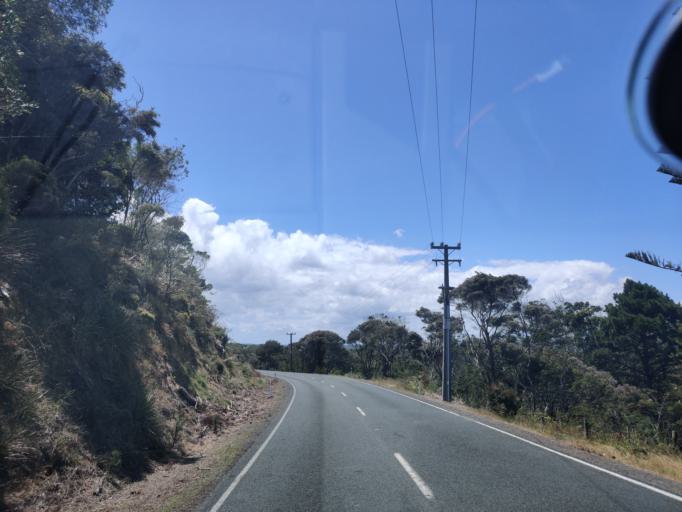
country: NZ
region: Northland
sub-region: Far North District
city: Kaitaia
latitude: -35.0240
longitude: 173.2121
